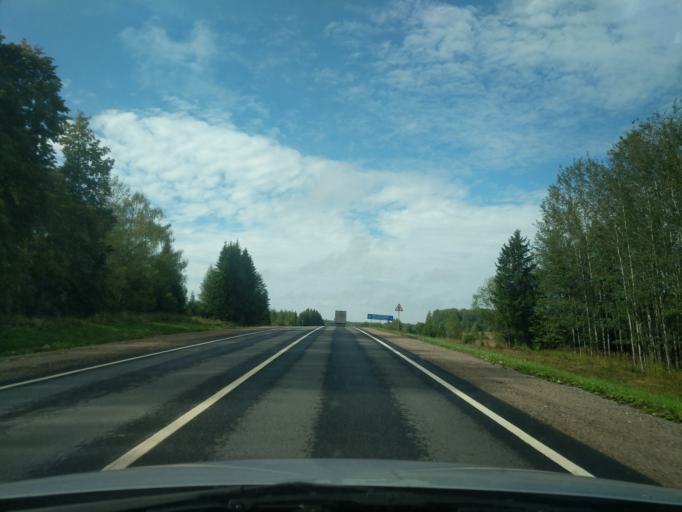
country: RU
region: Kostroma
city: Sudislavl'
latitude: 57.8406
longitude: 41.8449
